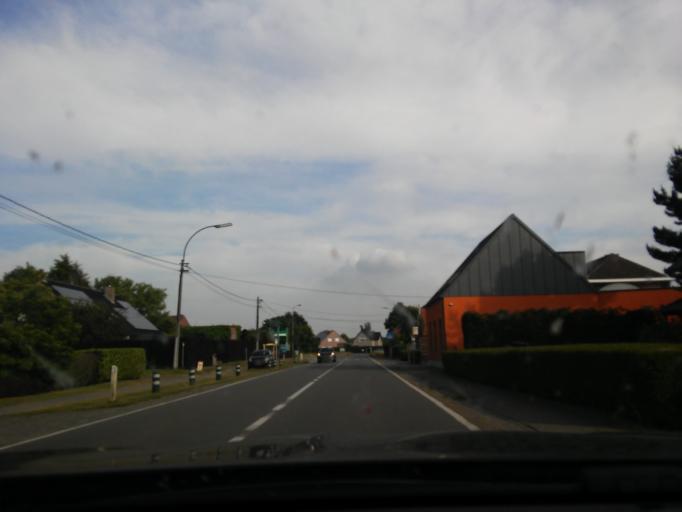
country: BE
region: Flanders
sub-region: Provincie Oost-Vlaanderen
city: Assenede
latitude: 51.2064
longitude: 3.7646
